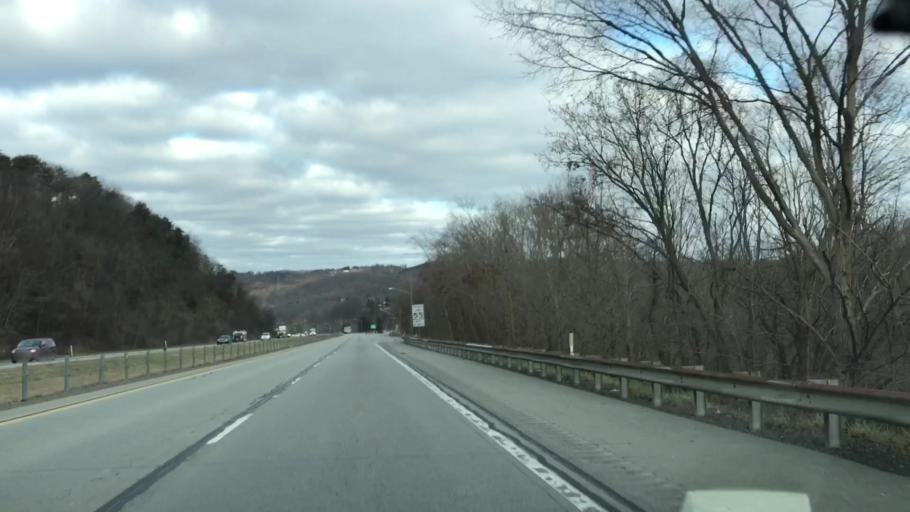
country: US
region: Pennsylvania
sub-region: Beaver County
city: Aliquippa
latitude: 40.5942
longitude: -80.2957
